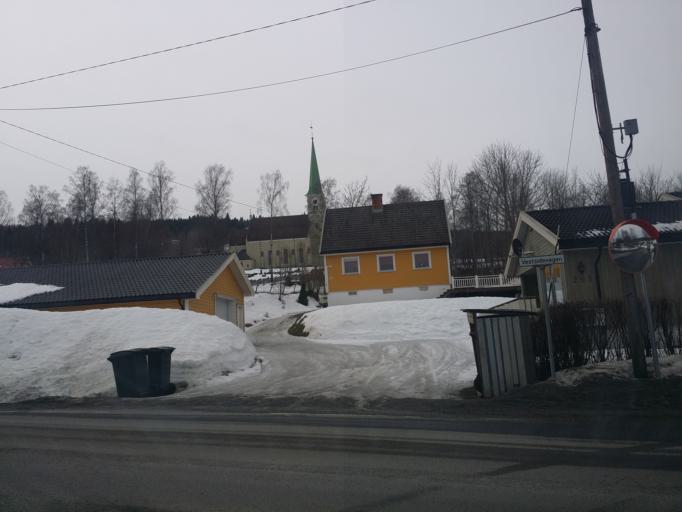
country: NO
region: Buskerud
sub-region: Lier
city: Tranby
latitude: 59.8513
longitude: 10.2163
